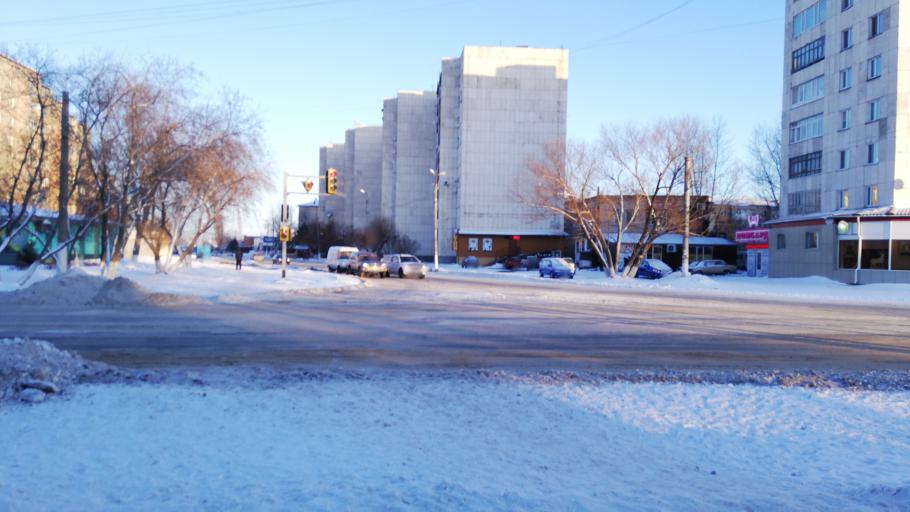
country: KZ
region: Soltustik Qazaqstan
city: Petropavlovsk
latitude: 54.8589
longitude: 69.1670
